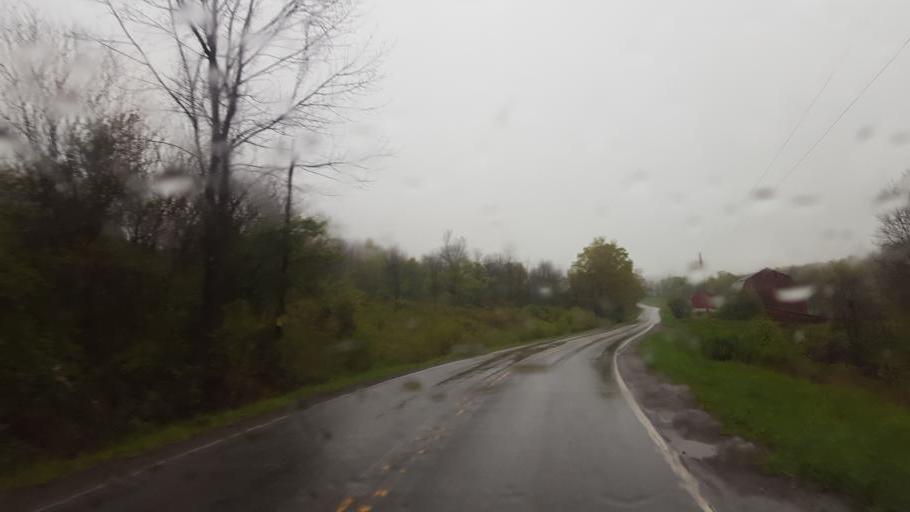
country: US
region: Pennsylvania
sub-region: Tioga County
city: Elkland
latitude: 42.0542
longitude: -77.4518
